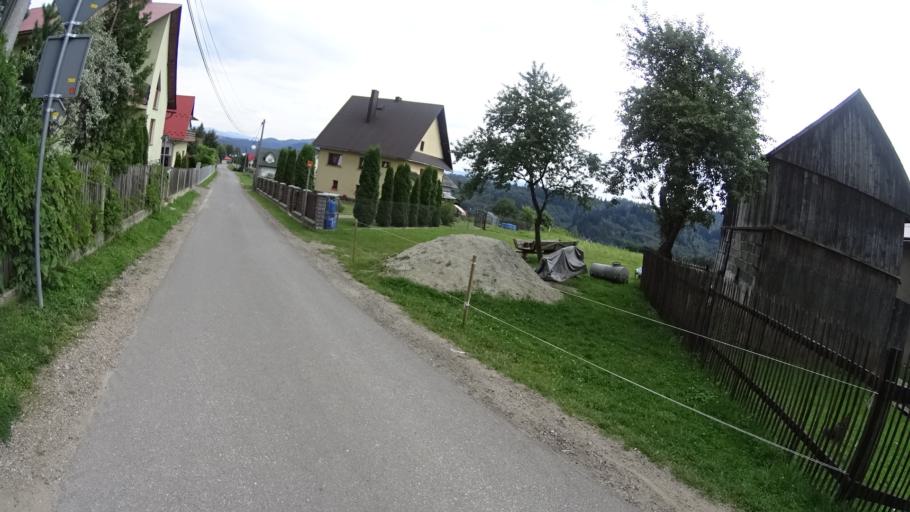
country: PL
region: Lesser Poland Voivodeship
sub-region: Powiat nowotarski
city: Maniowy
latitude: 49.4299
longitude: 20.2747
